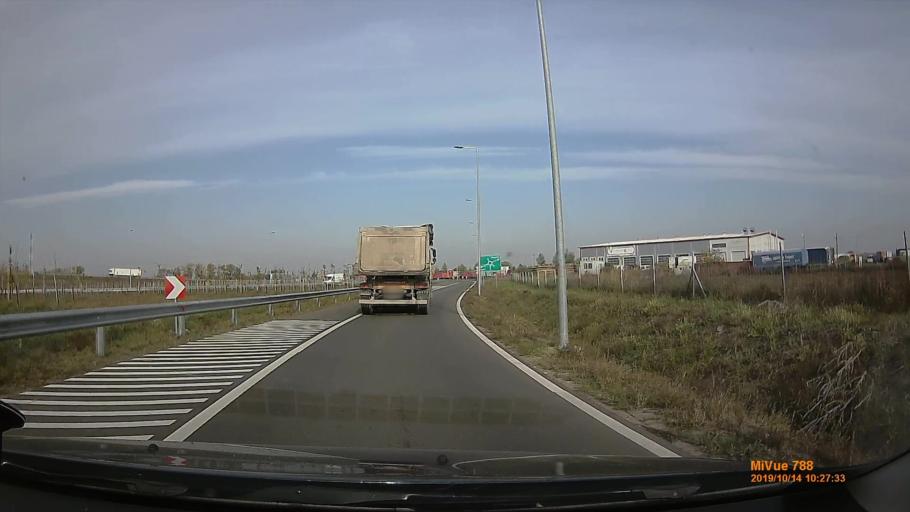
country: HU
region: Pest
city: Cegled
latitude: 47.1962
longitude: 19.8173
